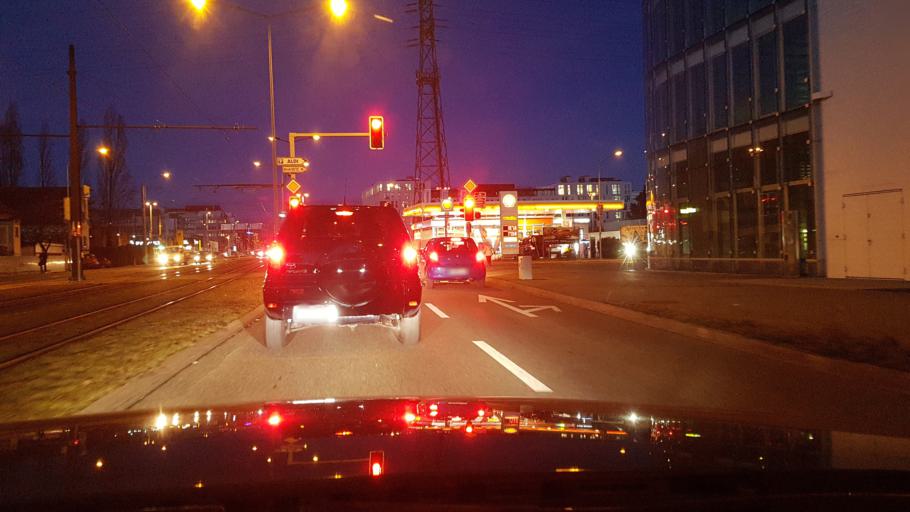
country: CH
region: Zurich
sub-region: Bezirk Zuerich
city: Zuerich (Kreis 11) / Seebach
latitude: 47.4192
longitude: 8.5556
